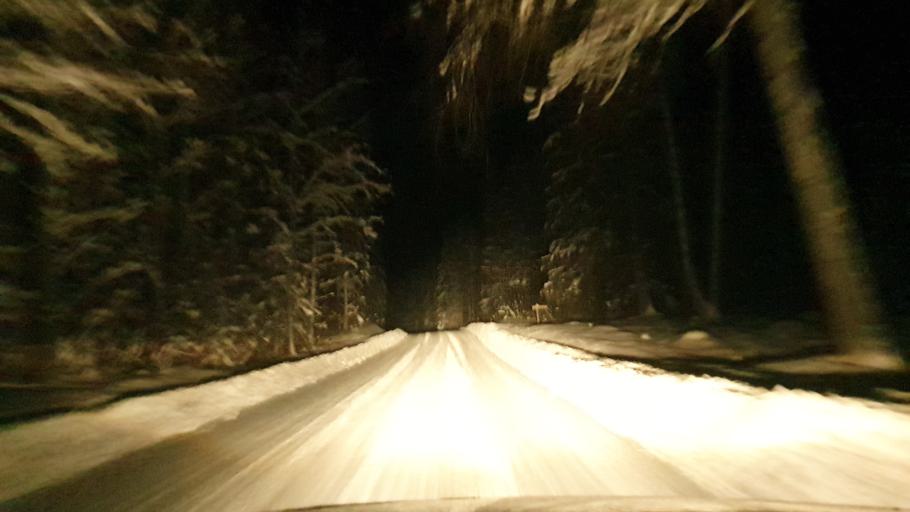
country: EE
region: Vorumaa
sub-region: Antsla vald
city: Vana-Antsla
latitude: 57.9675
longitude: 26.5981
